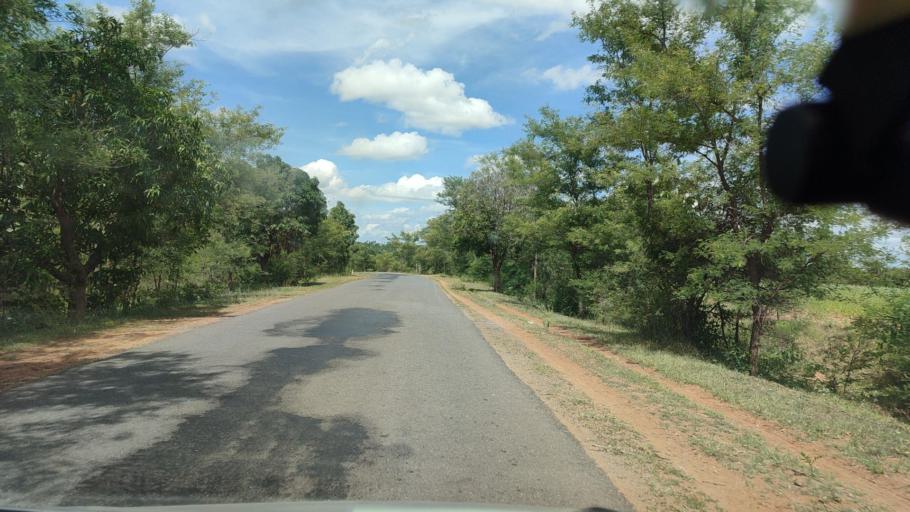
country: MM
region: Magway
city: Magway
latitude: 20.1880
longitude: 95.1362
